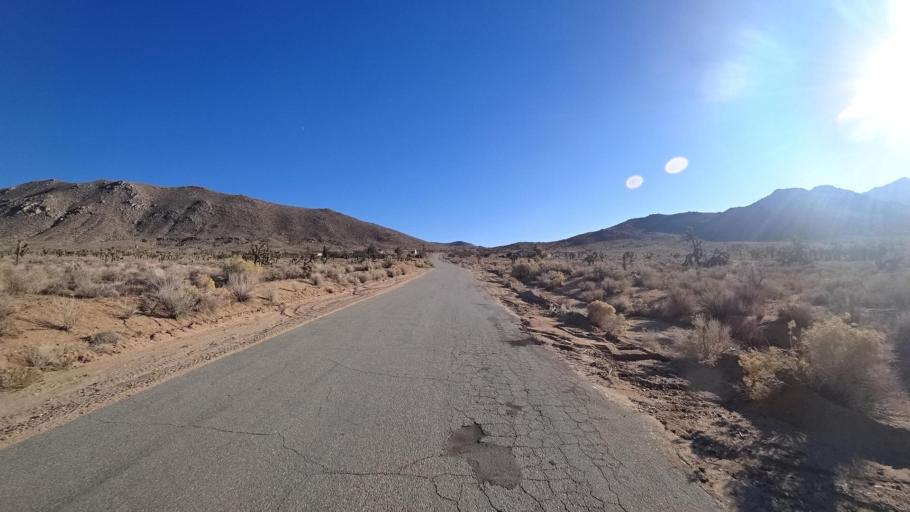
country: US
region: California
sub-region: Kern County
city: Weldon
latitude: 35.5375
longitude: -118.2039
